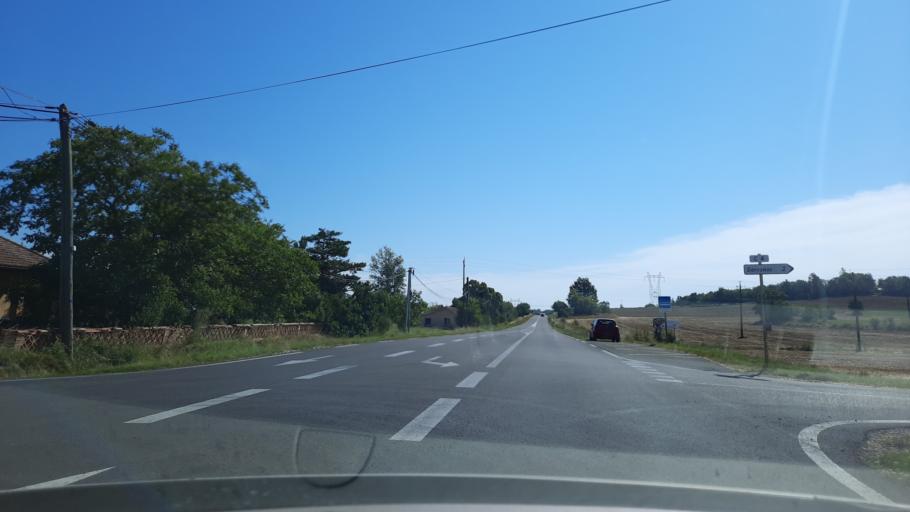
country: FR
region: Midi-Pyrenees
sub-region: Departement du Tarn-et-Garonne
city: Septfonds
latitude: 44.1917
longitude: 1.6748
